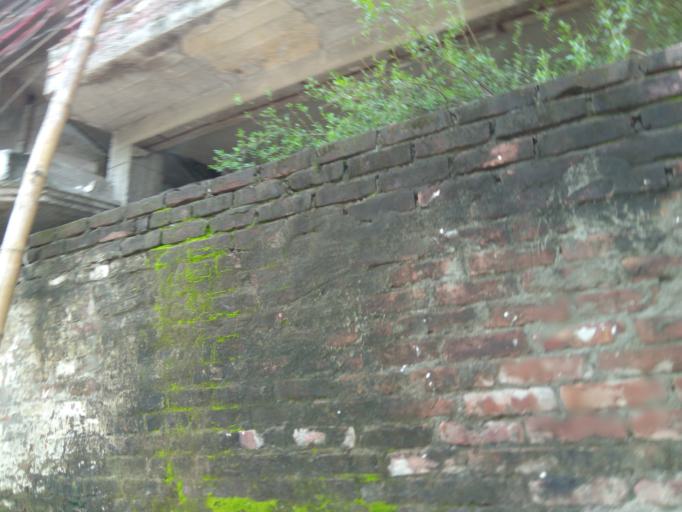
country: BD
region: Dhaka
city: Azimpur
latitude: 23.7291
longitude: 90.3605
